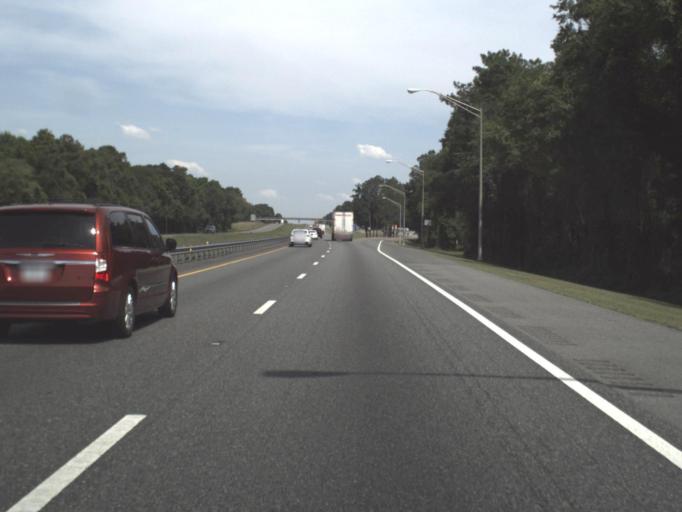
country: US
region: Florida
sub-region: Suwannee County
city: Wellborn
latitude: 30.2755
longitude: -82.8047
